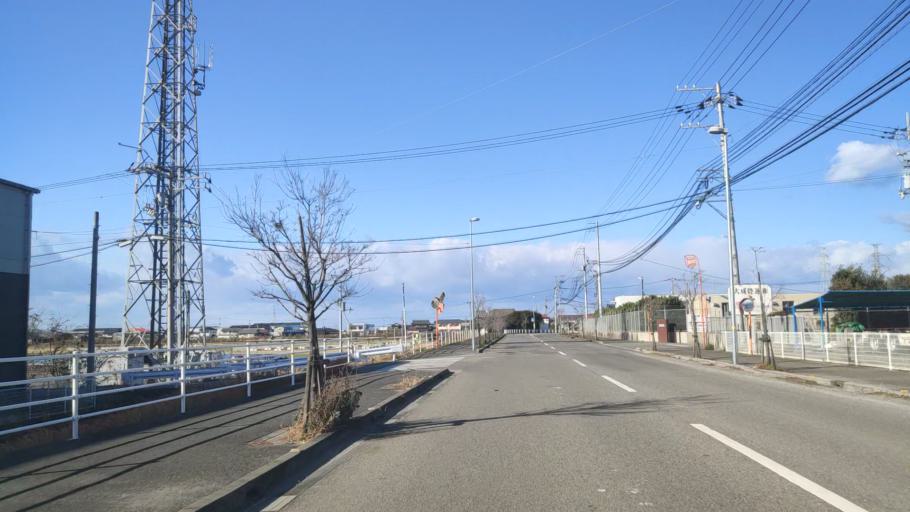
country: JP
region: Ehime
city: Saijo
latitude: 33.9272
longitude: 133.1661
